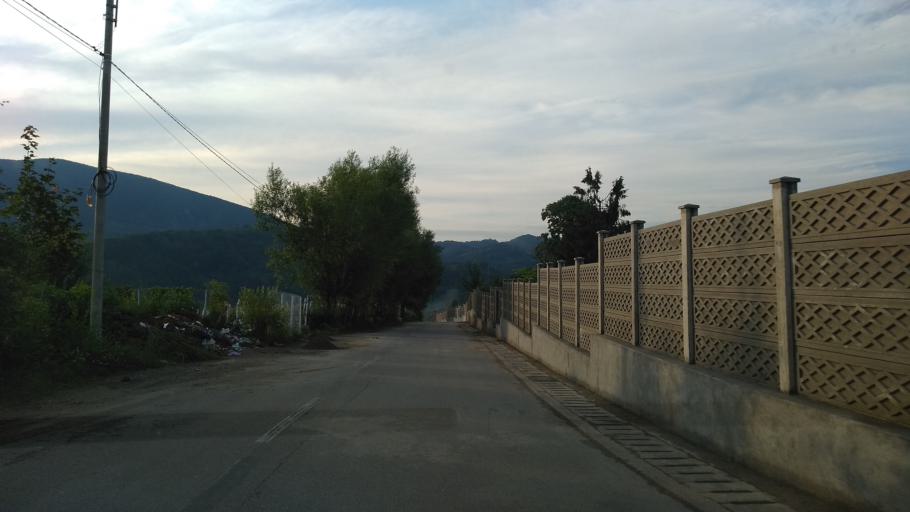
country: RO
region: Hunedoara
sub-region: Municipiul  Vulcan
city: Jiu-Paroseni
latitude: 45.3668
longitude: 23.2833
